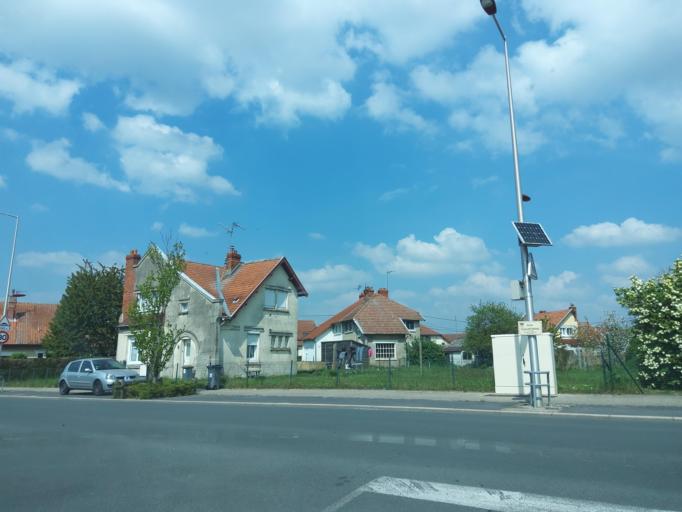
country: FR
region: Picardie
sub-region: Departement de l'Aisne
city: Laon
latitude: 49.5758
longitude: 3.6332
